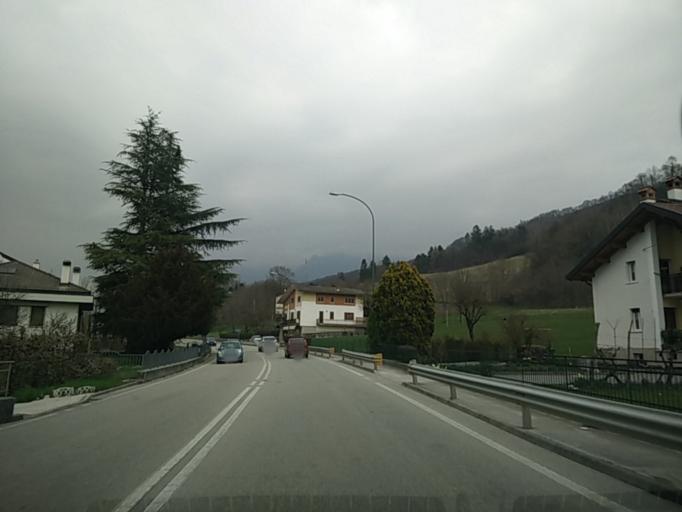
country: IT
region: Veneto
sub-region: Provincia di Belluno
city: Ponte nell'Alpi
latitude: 46.1534
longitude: 12.2641
